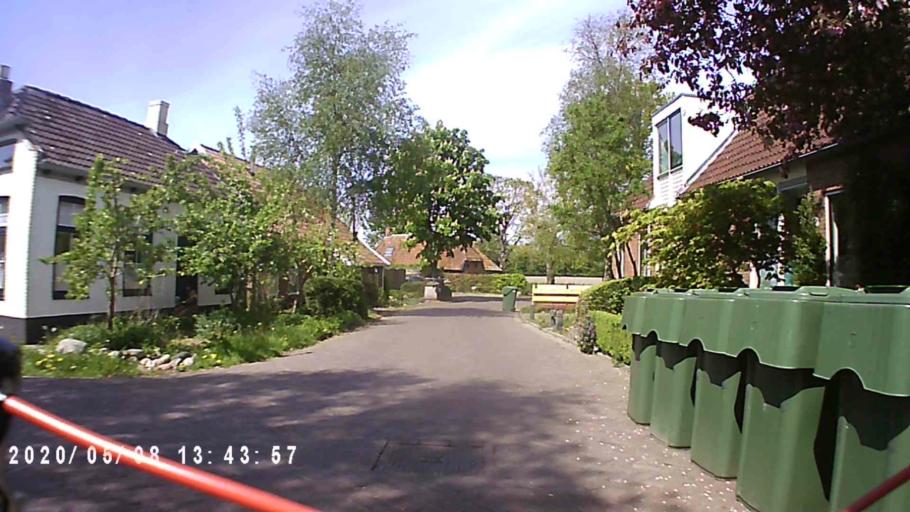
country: NL
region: Groningen
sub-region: Gemeente Appingedam
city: Appingedam
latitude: 53.3242
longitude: 6.7857
